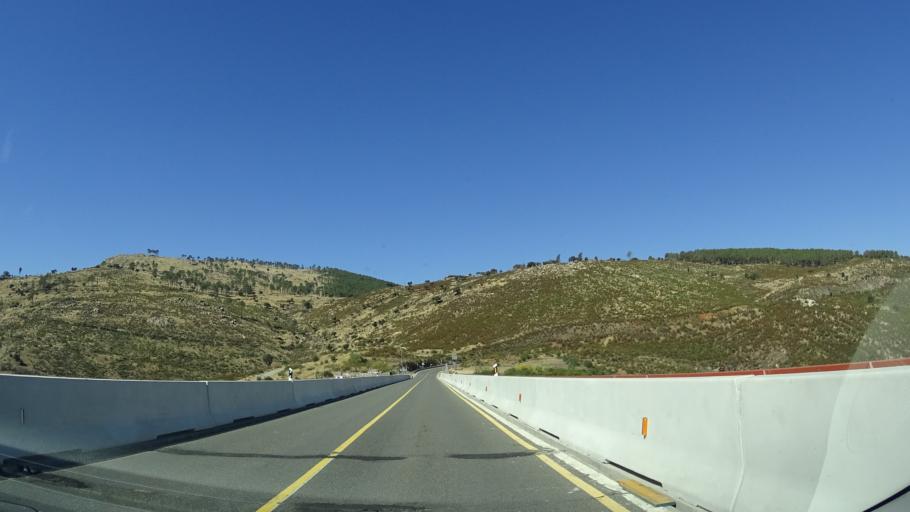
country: ES
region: Madrid
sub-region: Provincia de Madrid
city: Santa Maria de la Alameda
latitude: 40.5543
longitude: -4.2685
